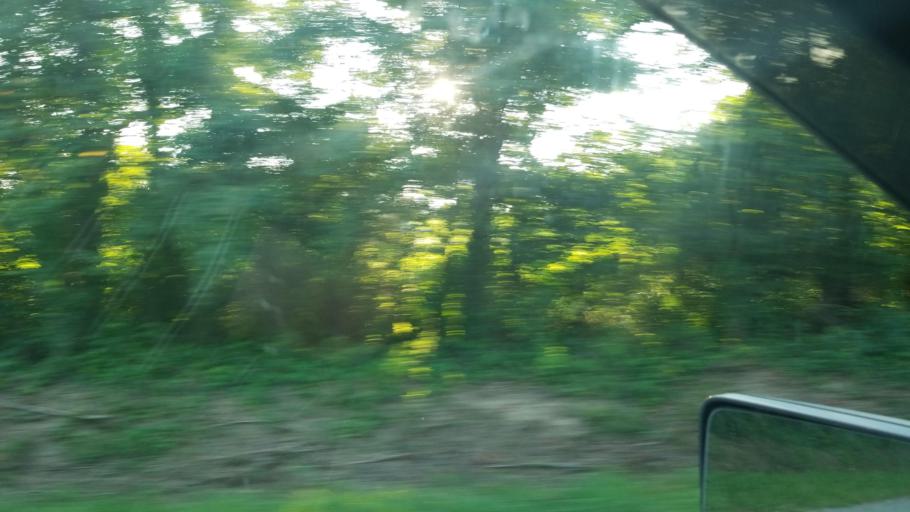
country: US
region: Illinois
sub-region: Saline County
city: Harrisburg
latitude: 37.7567
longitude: -88.5679
